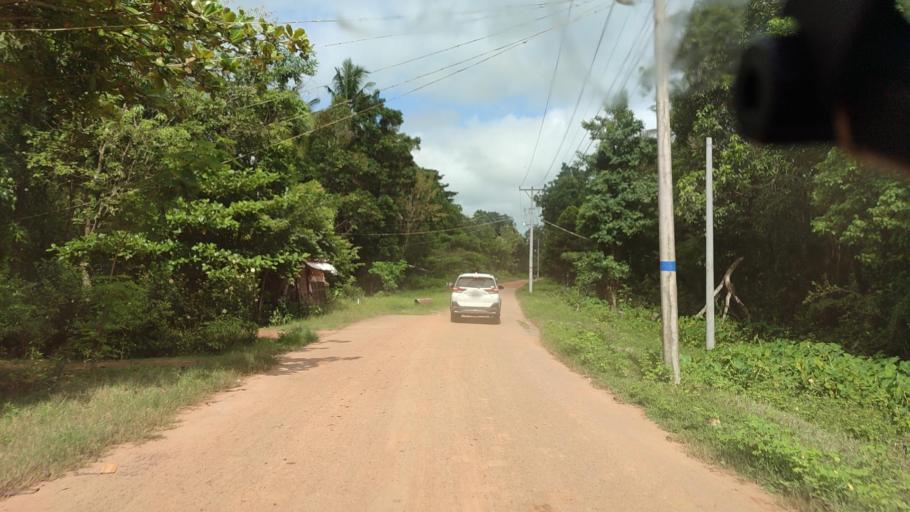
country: MM
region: Bago
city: Letpandan
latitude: 17.8952
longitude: 95.7158
